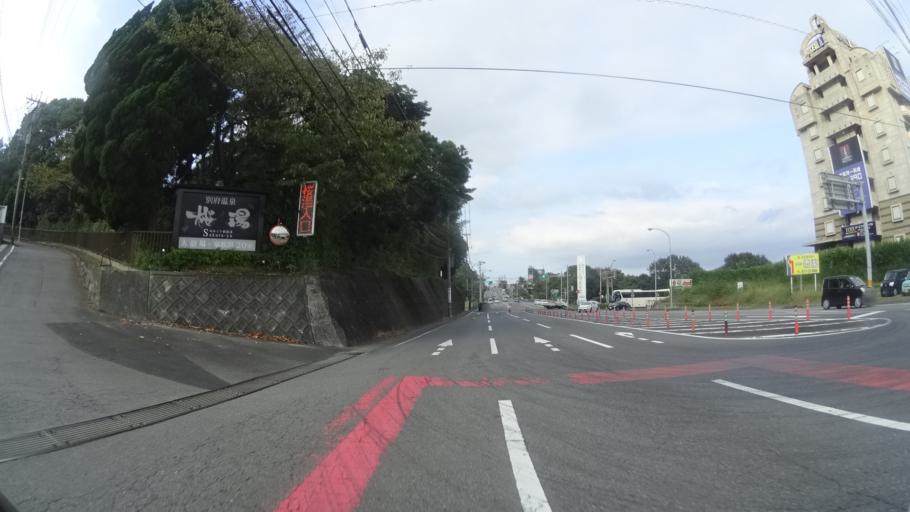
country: JP
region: Oita
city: Beppu
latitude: 33.2917
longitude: 131.4599
